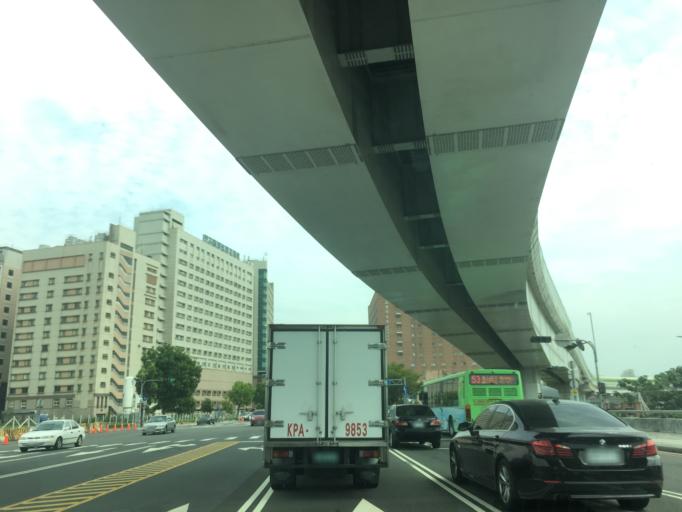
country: TW
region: Taiwan
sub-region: Taichung City
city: Taichung
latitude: 24.1233
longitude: 120.6481
